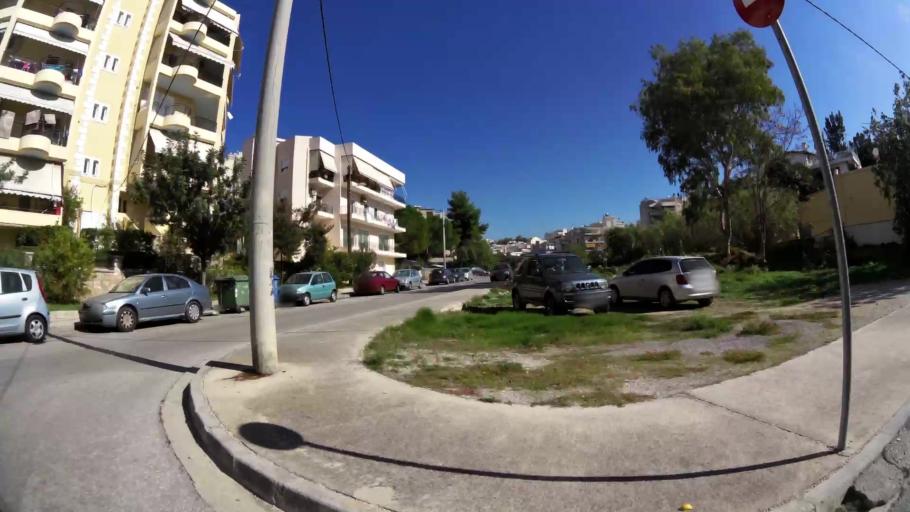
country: GR
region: Attica
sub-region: Nomarchia Athinas
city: Metamorfosi
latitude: 38.0603
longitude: 23.7659
